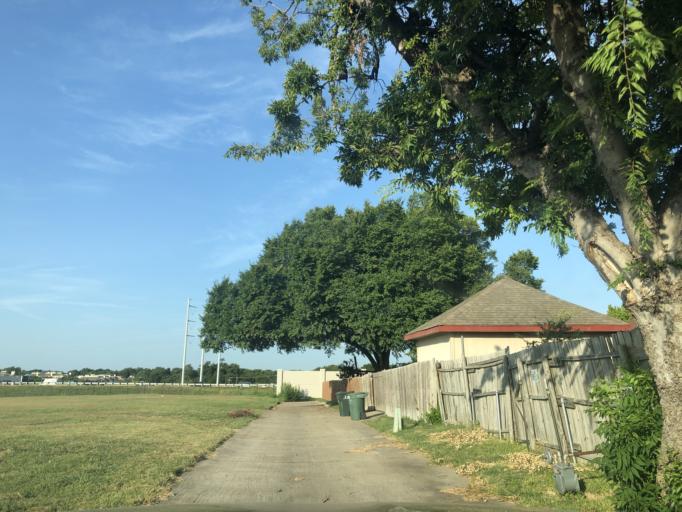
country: US
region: Texas
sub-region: Dallas County
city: Garland
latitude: 32.8457
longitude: -96.6341
